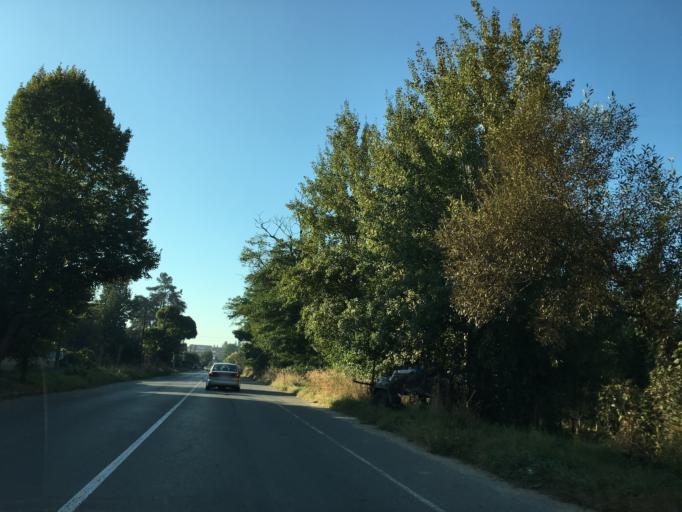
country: BG
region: Sofiya
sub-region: Obshtina Ikhtiman
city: Ikhtiman
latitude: 42.3919
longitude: 23.8708
